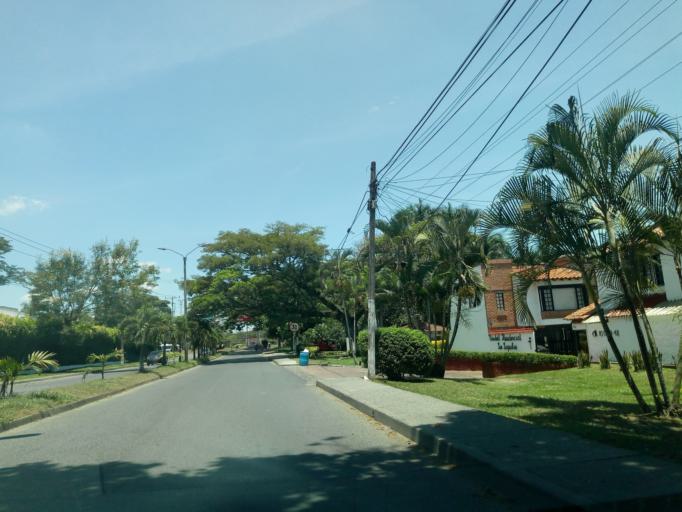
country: CO
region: Valle del Cauca
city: Cartago
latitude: 4.7340
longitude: -75.9111
